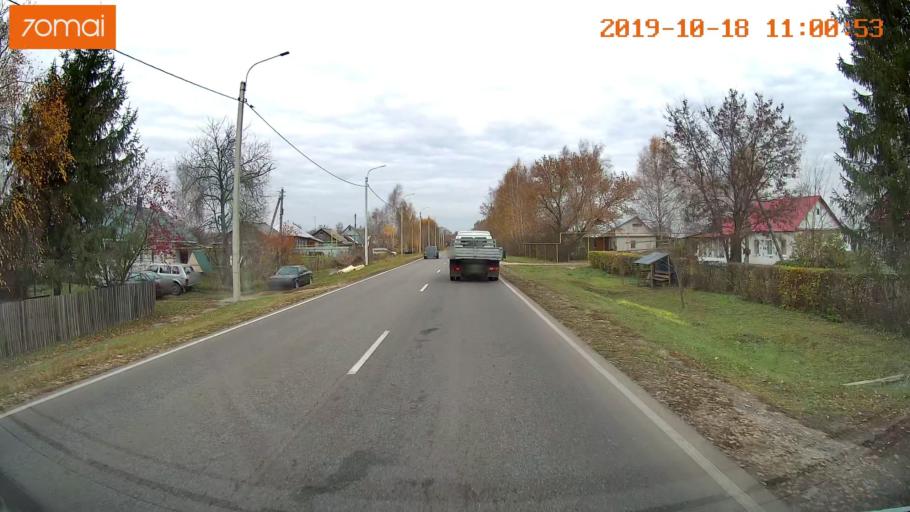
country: RU
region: Tula
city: Yepifan'
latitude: 53.8482
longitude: 38.5528
